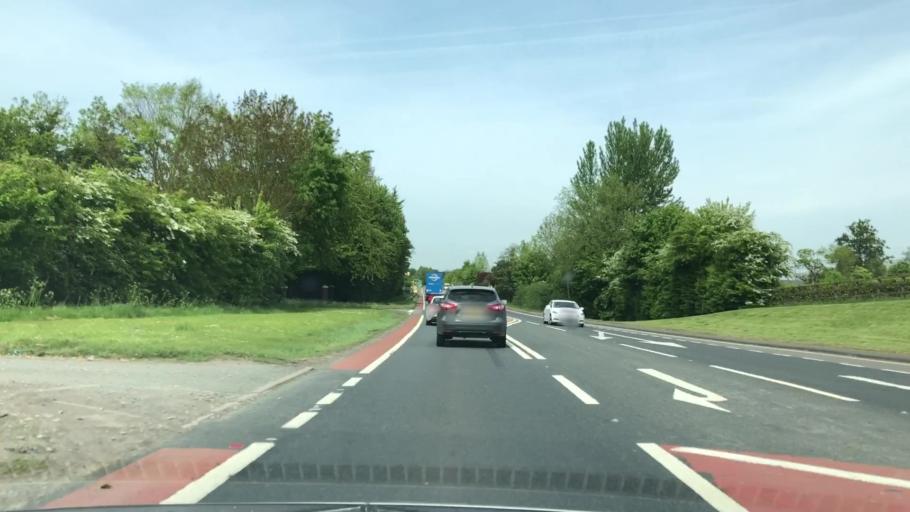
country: GB
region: England
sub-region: Shropshire
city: Gobowen
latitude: 52.9116
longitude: -3.0422
